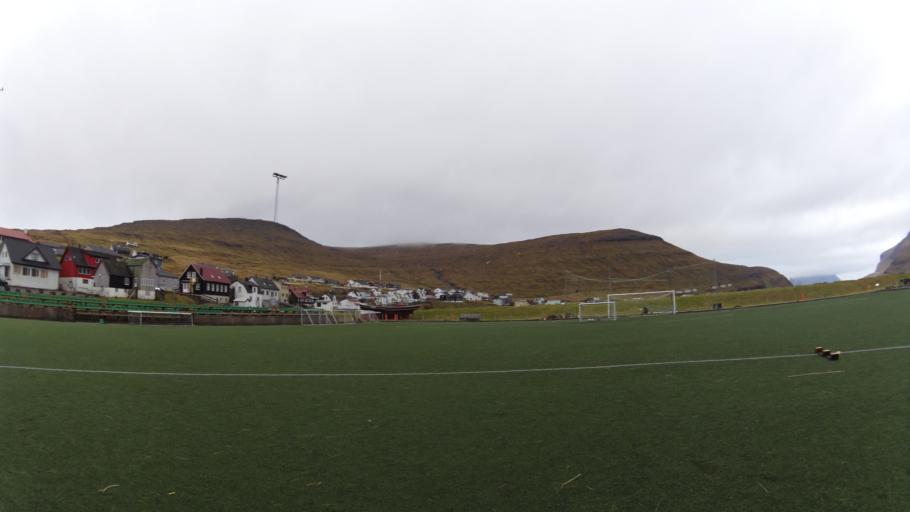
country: FO
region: Vagar
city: Sorvagur
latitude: 62.0716
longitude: -7.3103
